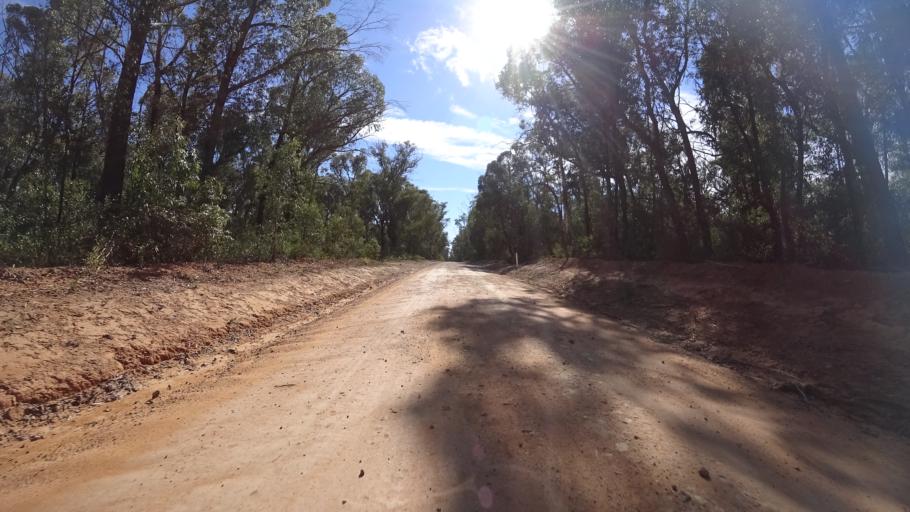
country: AU
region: New South Wales
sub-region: Lithgow
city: Lithgow
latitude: -33.4301
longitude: 150.1960
